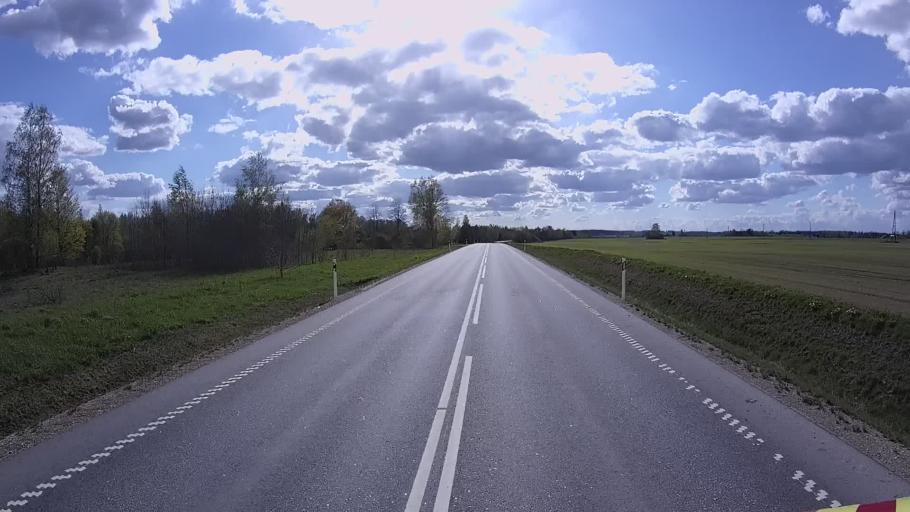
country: EE
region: Jogevamaa
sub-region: Mustvee linn
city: Mustvee
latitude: 58.8329
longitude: 26.7961
